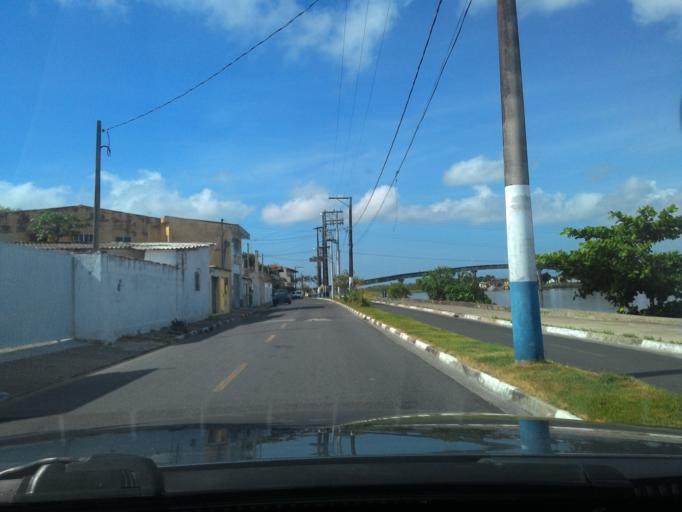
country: BR
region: Sao Paulo
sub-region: Iguape
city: Iguape
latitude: -24.7108
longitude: -47.5624
